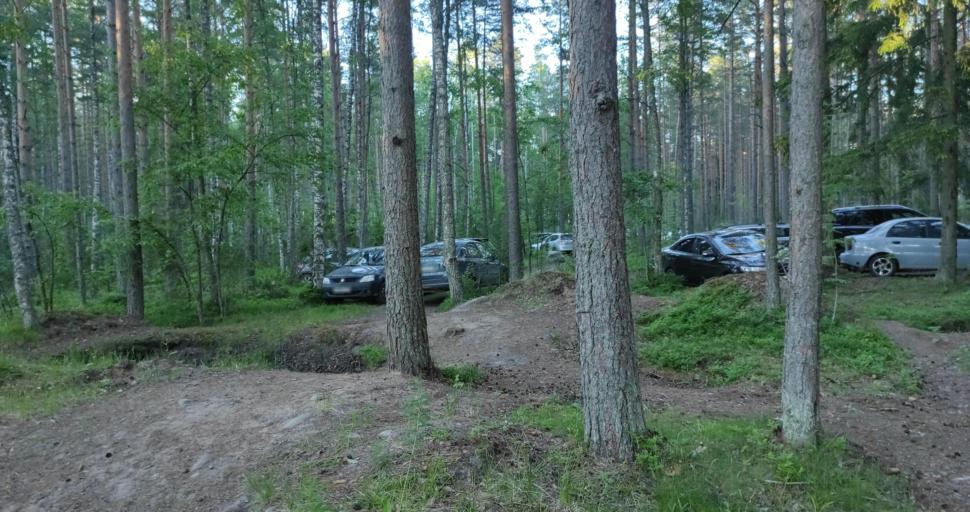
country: RU
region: Leningrad
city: Sosnovyy Bor
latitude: 60.1639
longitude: 29.1494
